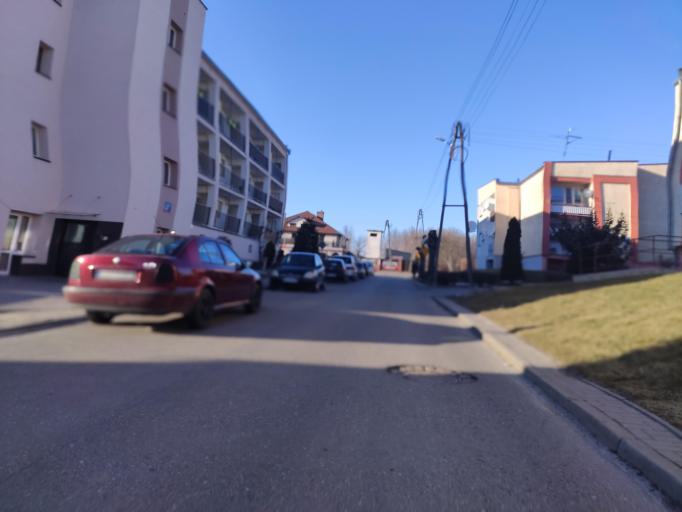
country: PL
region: Lublin Voivodeship
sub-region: Powiat lubartowski
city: Kock
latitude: 51.6403
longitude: 22.4465
